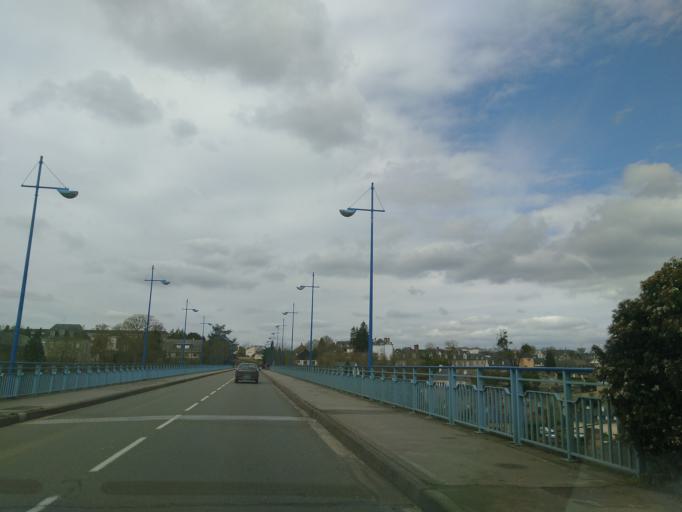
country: FR
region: Pays de la Loire
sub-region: Departement de la Mayenne
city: Mayenne
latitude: 48.2991
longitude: -0.6183
